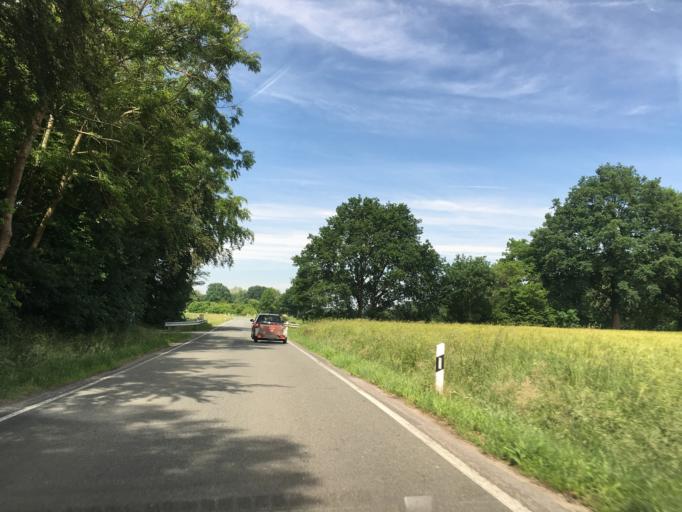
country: DE
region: North Rhine-Westphalia
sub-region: Regierungsbezirk Munster
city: Nordwalde
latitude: 52.1266
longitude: 7.4410
